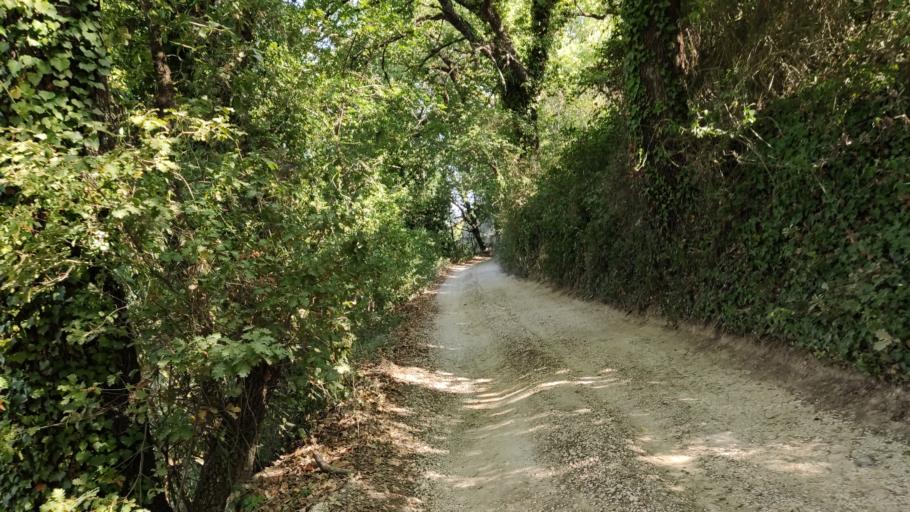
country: IT
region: Umbria
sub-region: Provincia di Terni
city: Amelia
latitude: 42.5310
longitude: 12.4100
